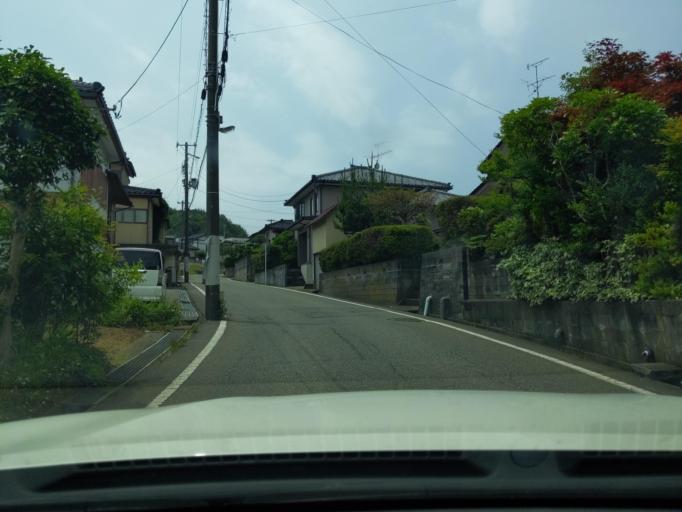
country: JP
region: Niigata
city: Kashiwazaki
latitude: 37.3537
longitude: 138.5444
